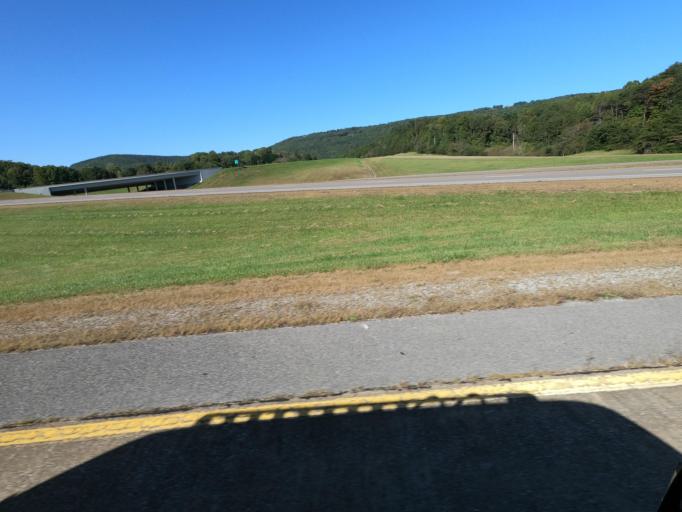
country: US
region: Tennessee
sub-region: Hamilton County
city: Soddy-Daisy
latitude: 35.3025
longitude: -85.1486
